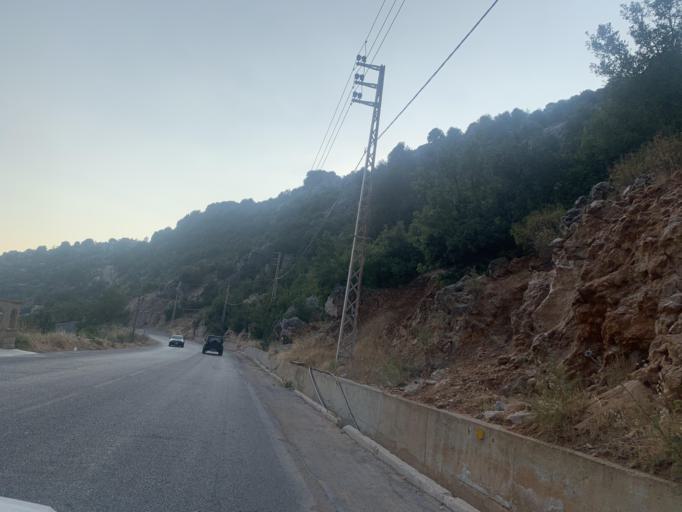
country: LB
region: Liban-Nord
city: Amioun
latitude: 34.1333
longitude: 35.8183
